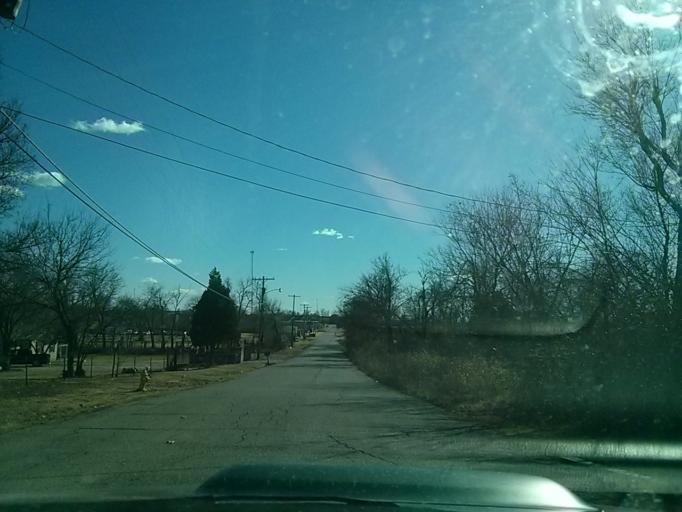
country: US
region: Oklahoma
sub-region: Tulsa County
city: Turley
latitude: 36.2100
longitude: -95.9515
